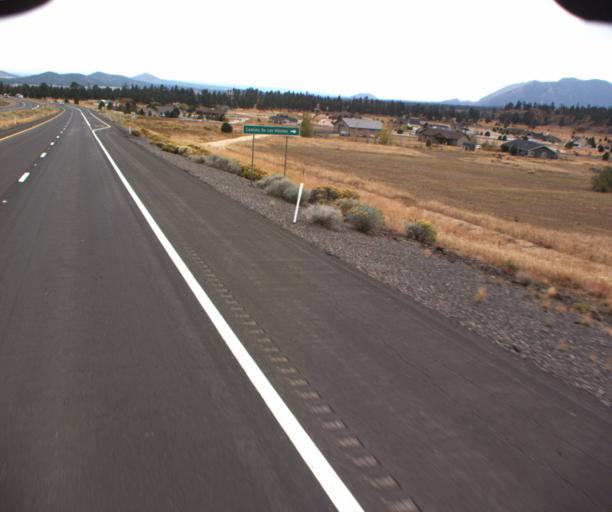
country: US
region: Arizona
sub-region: Coconino County
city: Flagstaff
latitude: 35.3470
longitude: -111.5629
